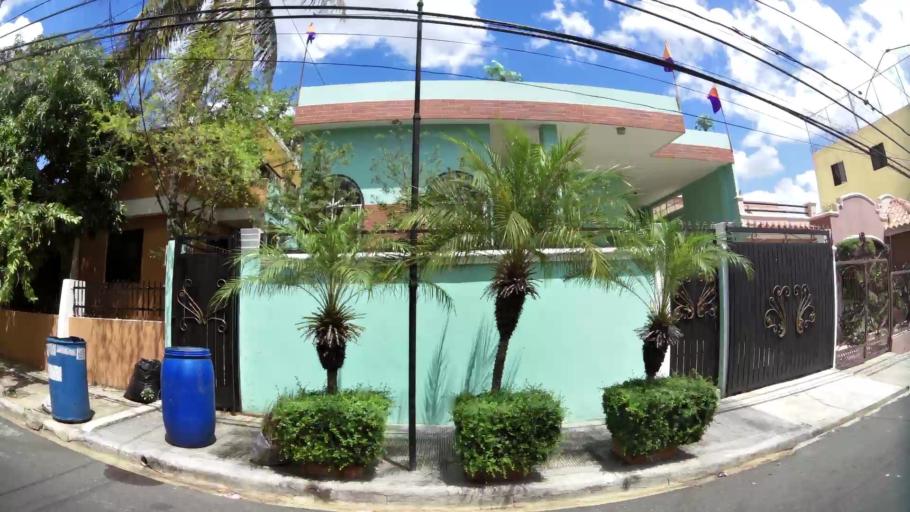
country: DO
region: Nacional
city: Ensanche Luperon
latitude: 18.5220
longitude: -69.9108
